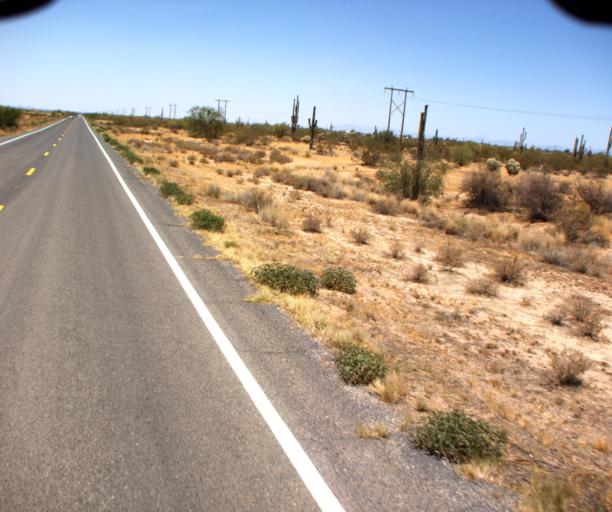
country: US
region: Arizona
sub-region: Pinal County
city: Florence
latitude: 32.9030
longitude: -111.2808
